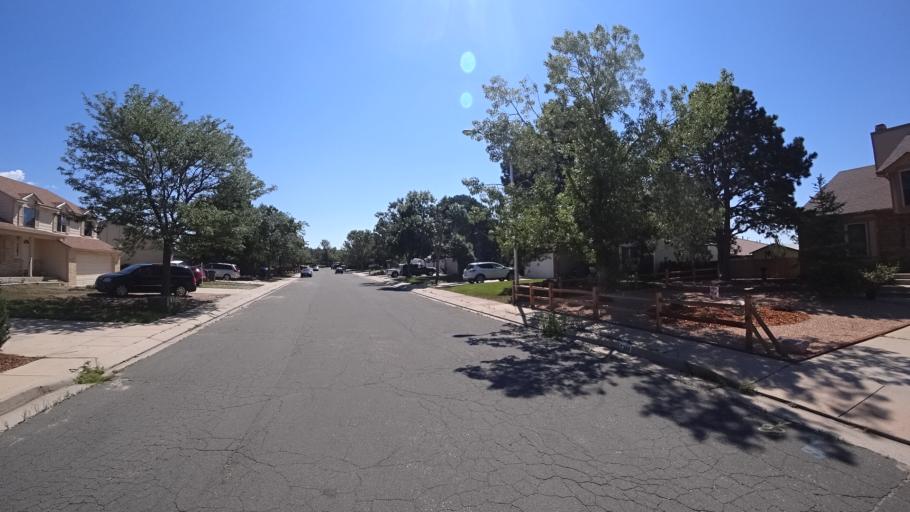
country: US
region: Colorado
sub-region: El Paso County
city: Black Forest
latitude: 38.9370
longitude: -104.7651
